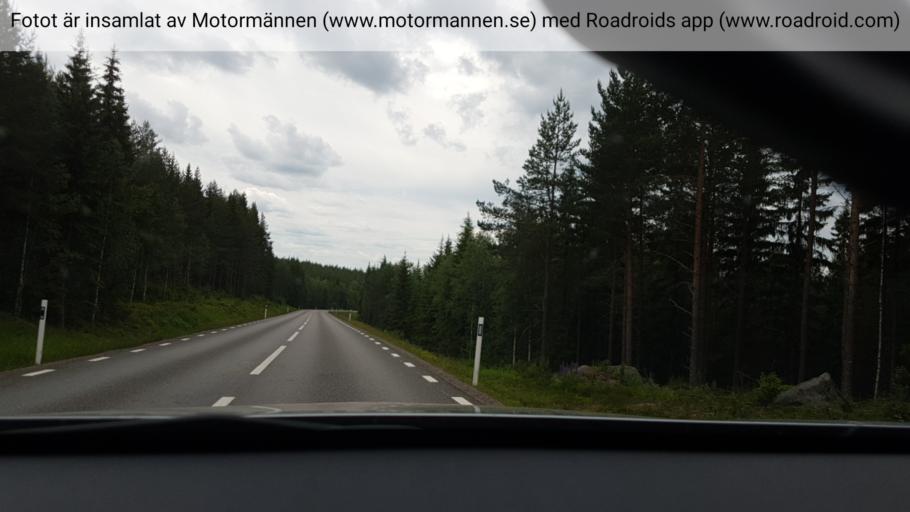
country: SE
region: Vaermland
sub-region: Torsby Kommun
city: Torsby
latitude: 60.3362
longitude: 13.1448
